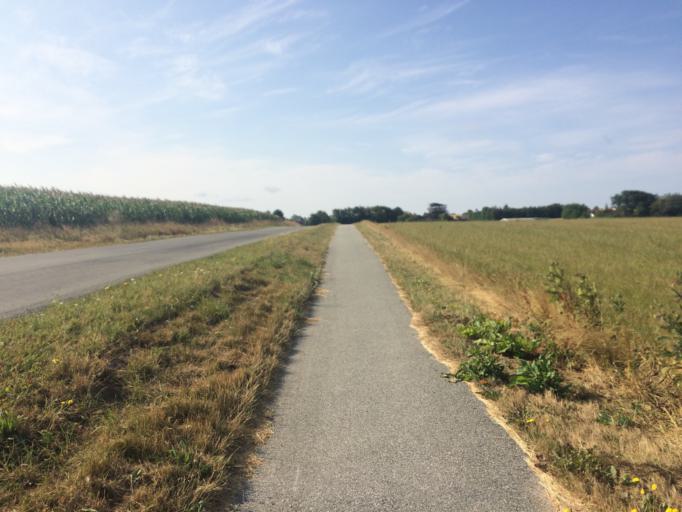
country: DK
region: Central Jutland
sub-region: Holstebro Kommune
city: Vinderup
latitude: 56.6045
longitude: 8.7715
